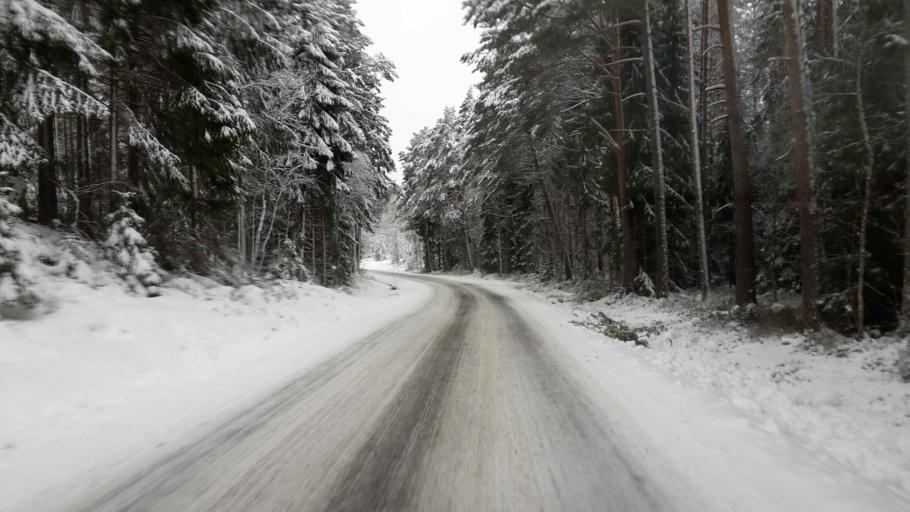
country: SE
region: Kalmar
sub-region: Vasterviks Kommun
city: Overum
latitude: 58.1512
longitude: 16.2452
